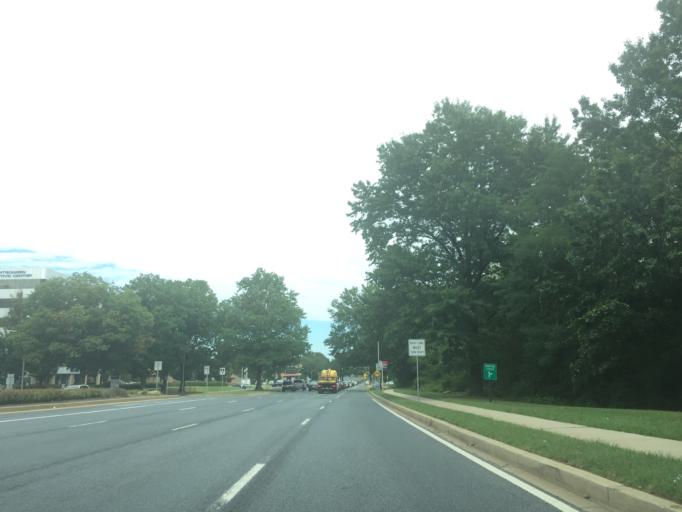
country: US
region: Maryland
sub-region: Montgomery County
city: Gaithersburg
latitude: 39.1531
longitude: -77.2111
